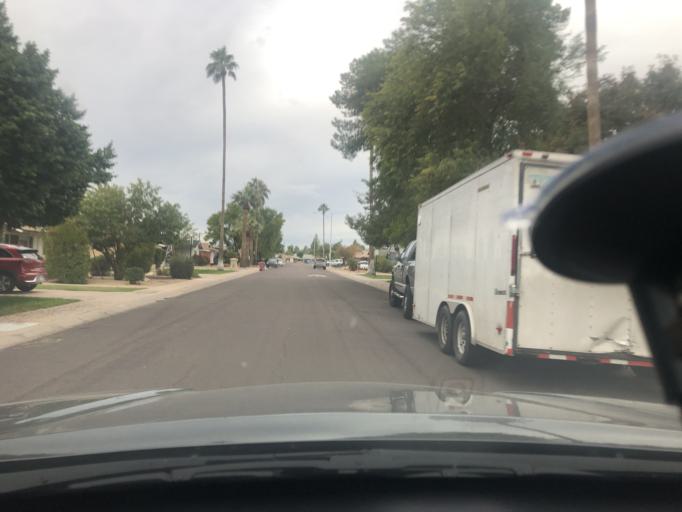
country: US
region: Arizona
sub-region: Maricopa County
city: Scottsdale
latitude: 33.4957
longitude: -111.9018
